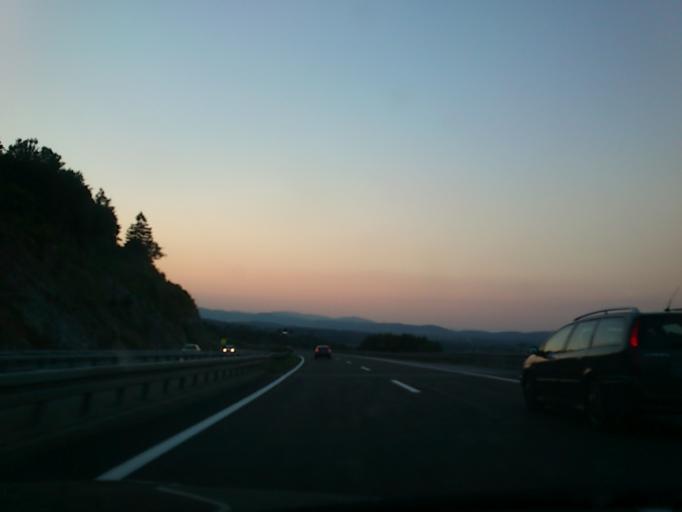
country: HR
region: Karlovacka
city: Ostarije
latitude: 45.1748
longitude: 15.2783
